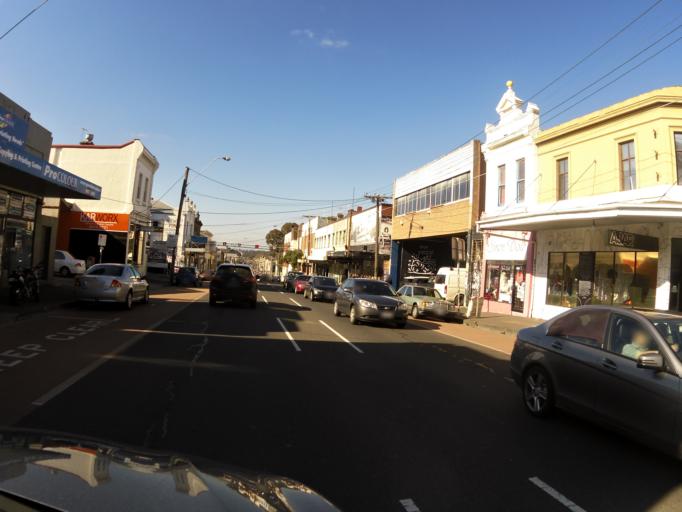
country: AU
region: Victoria
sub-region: Yarra
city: Collingwood
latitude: -37.7990
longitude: 144.9851
